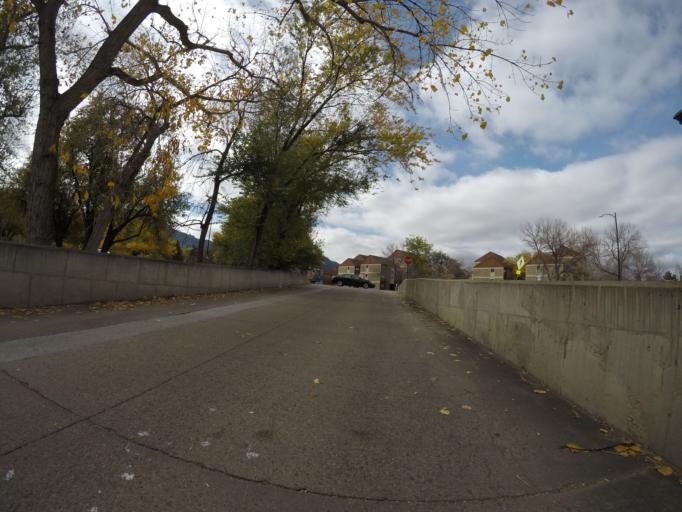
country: US
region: Colorado
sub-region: Boulder County
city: Boulder
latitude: 40.0131
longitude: -105.2627
